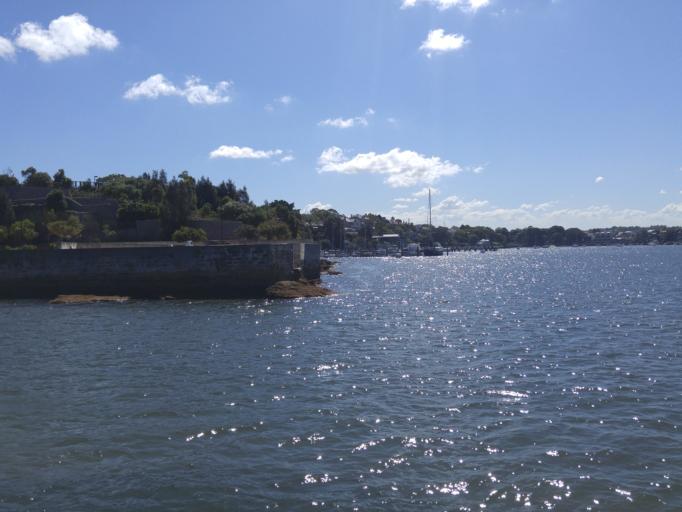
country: AU
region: New South Wales
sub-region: Leichhardt
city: Balmain East
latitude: -33.8518
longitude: 151.1912
